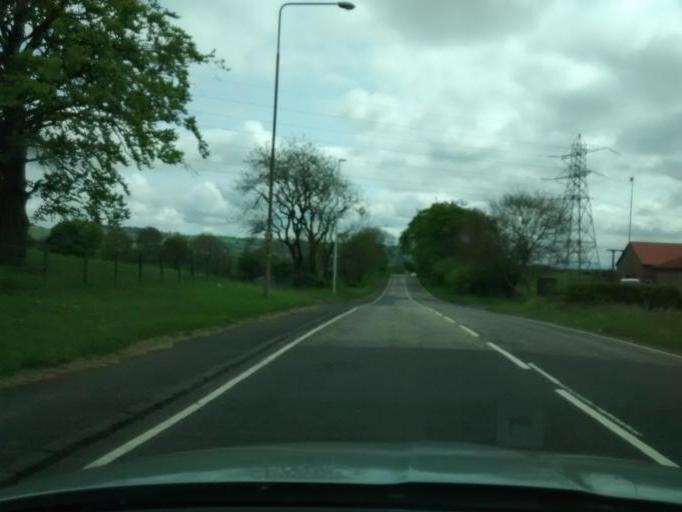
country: GB
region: Scotland
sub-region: West Lothian
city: Bathgate
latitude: 55.9003
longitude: -3.6743
